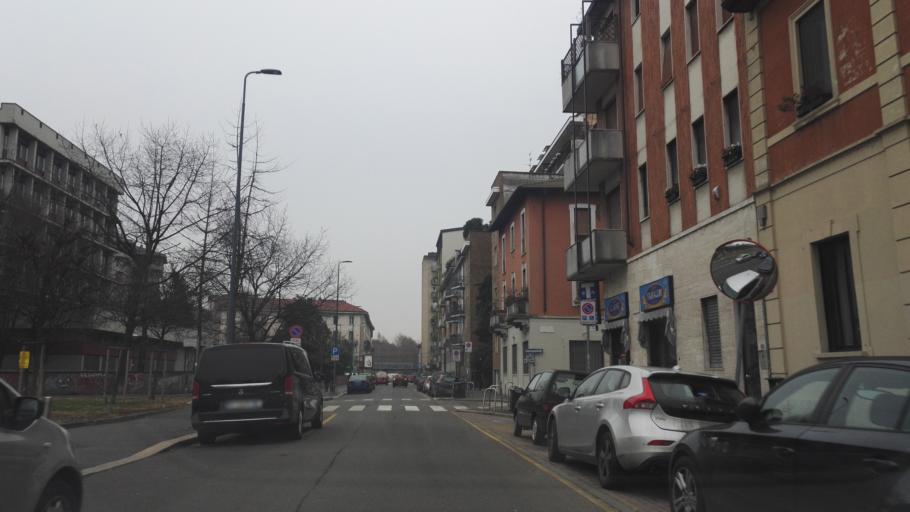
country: IT
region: Lombardy
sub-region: Citta metropolitana di Milano
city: Milano
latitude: 45.4457
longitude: 9.1824
